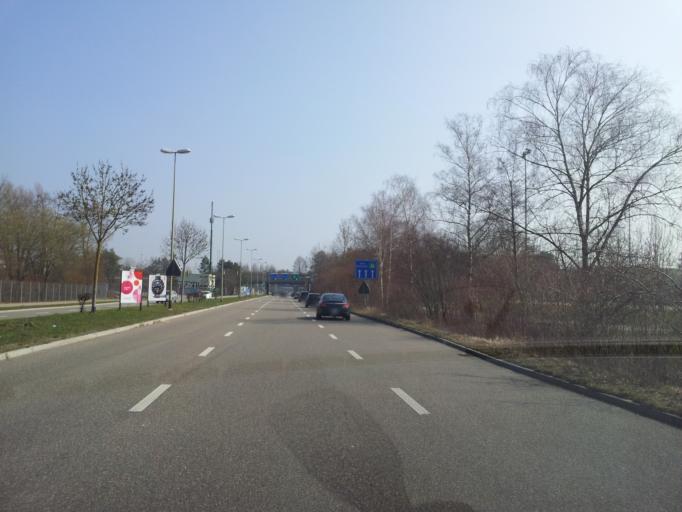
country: CH
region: Zurich
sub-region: Bezirk Zuerich
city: Zuerich (Kreis 12) / Hirzenbach
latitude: 47.4043
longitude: 8.5957
